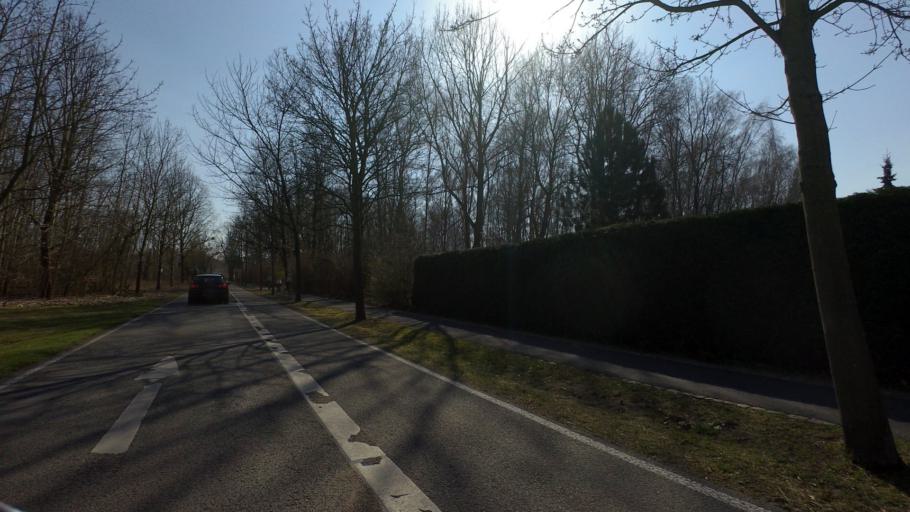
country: DE
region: Brandenburg
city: Hennigsdorf
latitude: 52.6031
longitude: 13.1980
